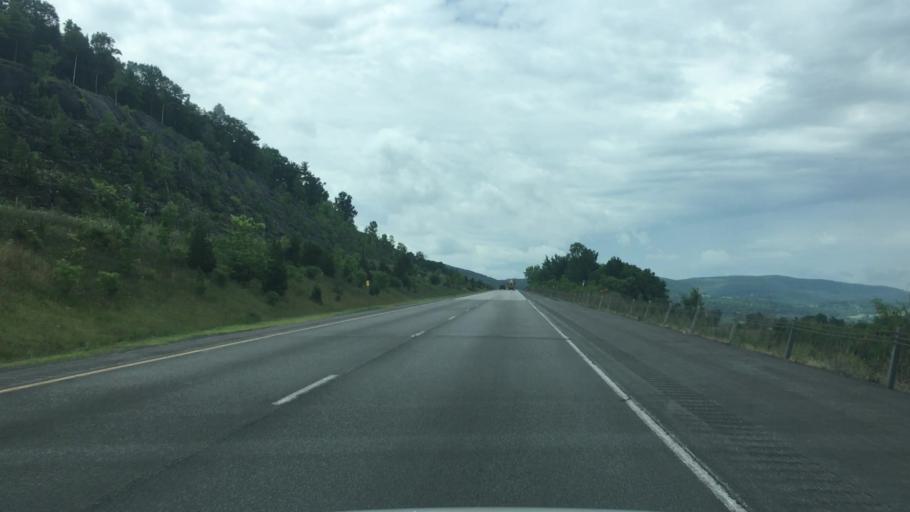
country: US
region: New York
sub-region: Schoharie County
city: Schoharie
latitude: 42.6966
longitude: -74.3473
